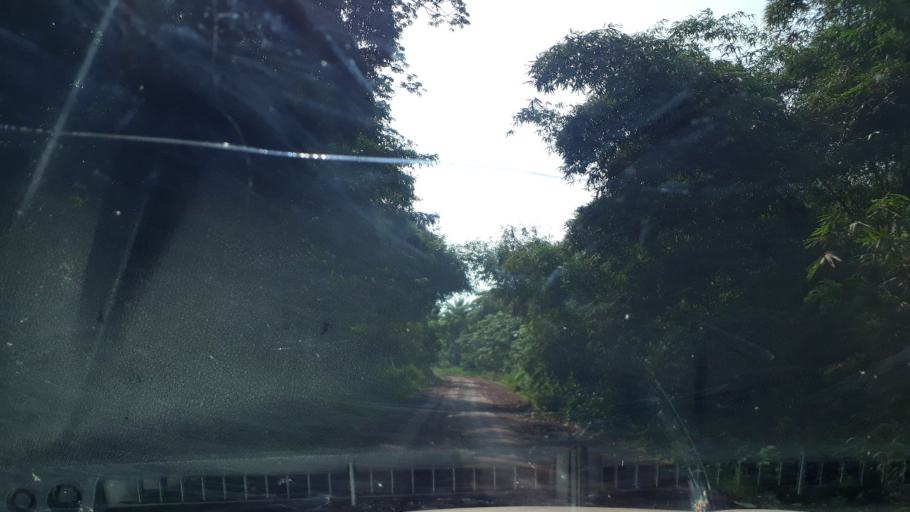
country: CD
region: Eastern Province
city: Wamba
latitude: 1.4132
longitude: 27.8134
